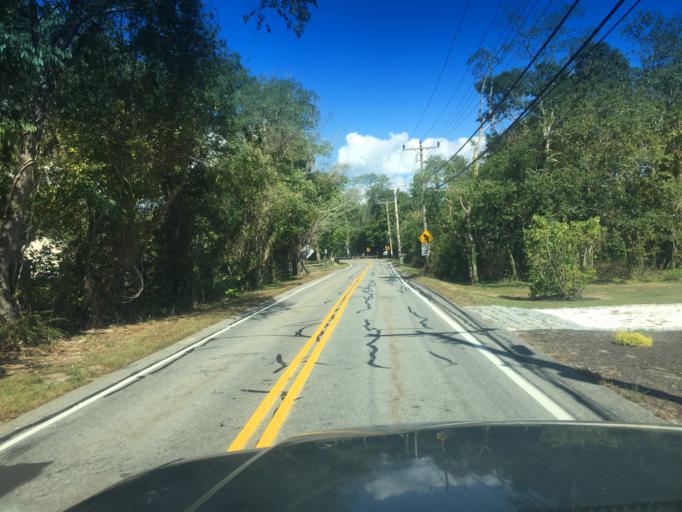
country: US
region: Massachusetts
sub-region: Barnstable County
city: Pocasset
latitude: 41.6658
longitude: -70.6072
